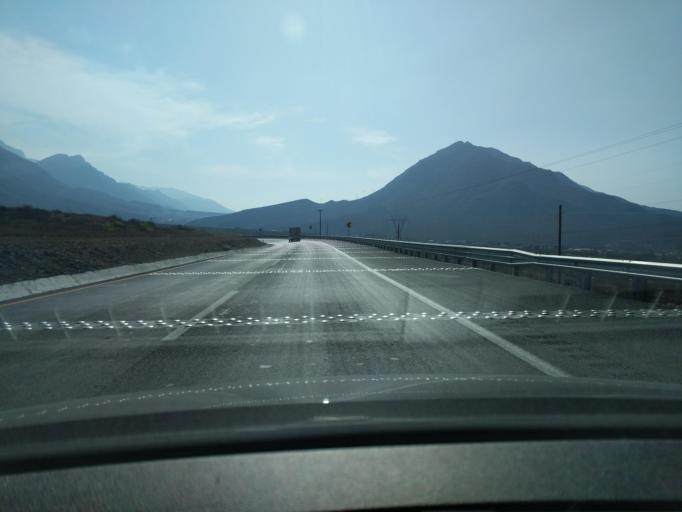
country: MX
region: Nuevo Leon
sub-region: Garcia
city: Las Torres de Guadalupe
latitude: 25.6686
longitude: -100.7040
